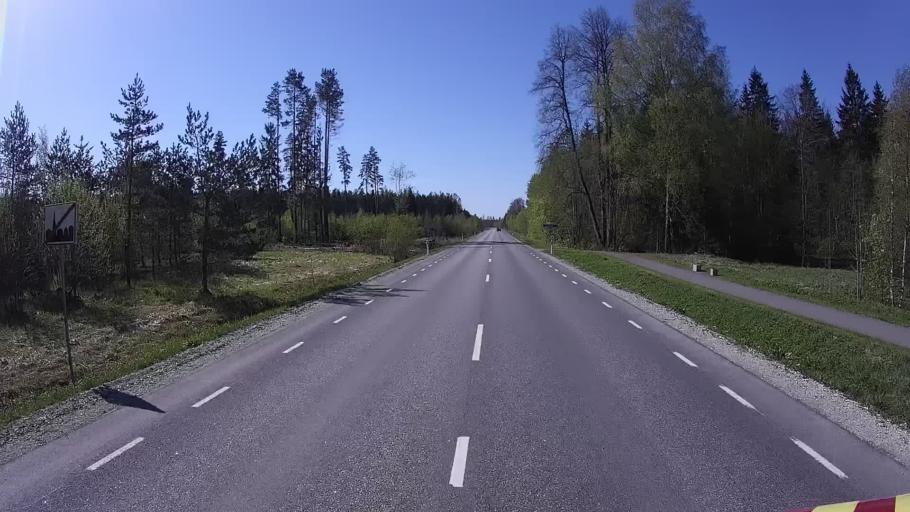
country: EE
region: Raplamaa
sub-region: Jaervakandi vald
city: Jarvakandi
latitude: 58.7663
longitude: 24.8149
